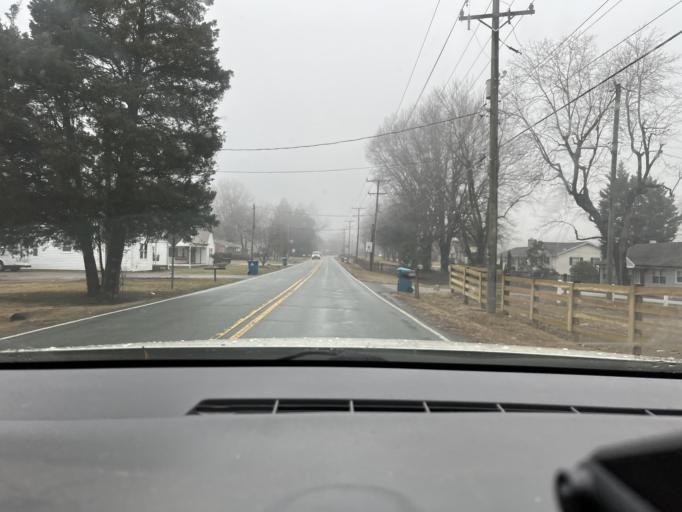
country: US
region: North Carolina
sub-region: Guilford County
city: Pleasant Garden
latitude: 35.9726
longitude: -79.7667
